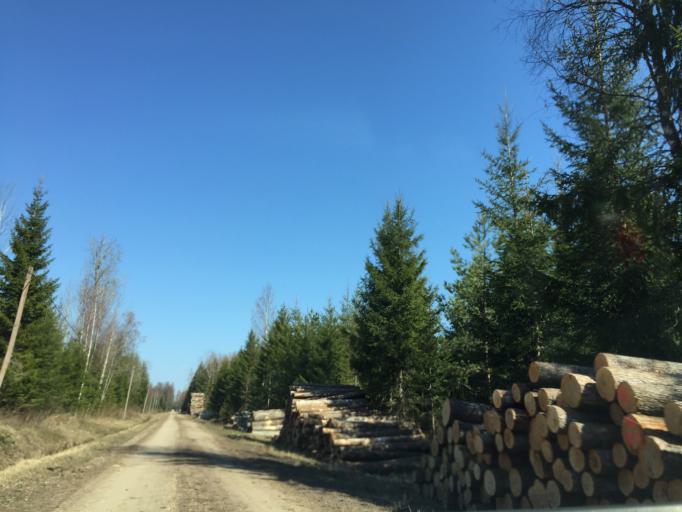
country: EE
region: Tartu
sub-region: Alatskivi vald
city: Kallaste
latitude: 58.5709
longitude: 26.9438
